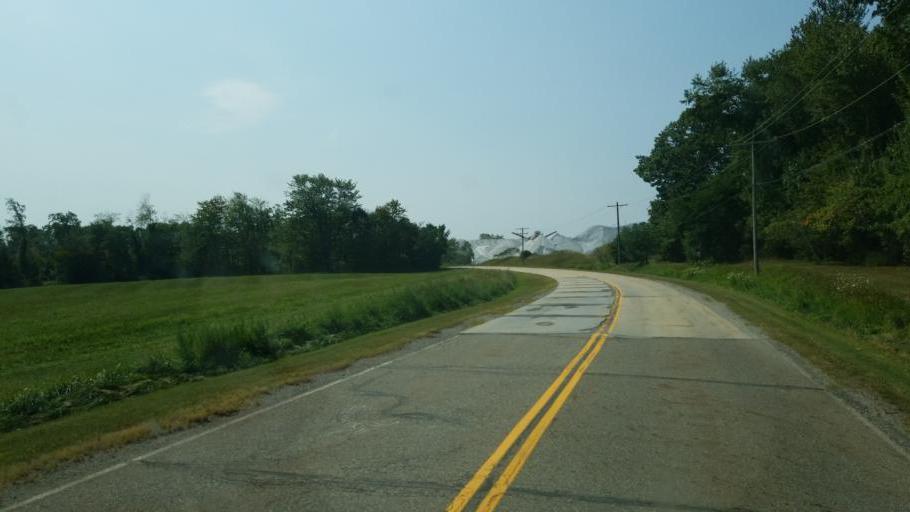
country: US
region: Ohio
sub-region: Lake County
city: Madison
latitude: 41.6737
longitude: -81.0379
